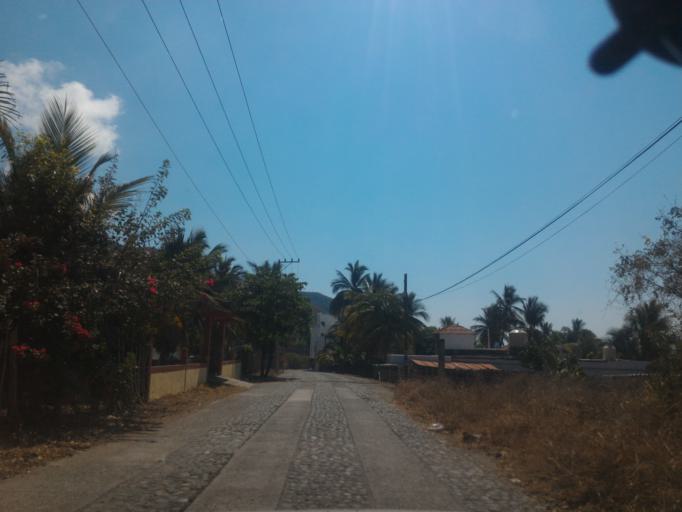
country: MX
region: Michoacan
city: Coahuayana Viejo
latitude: 18.5777
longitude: -103.6664
